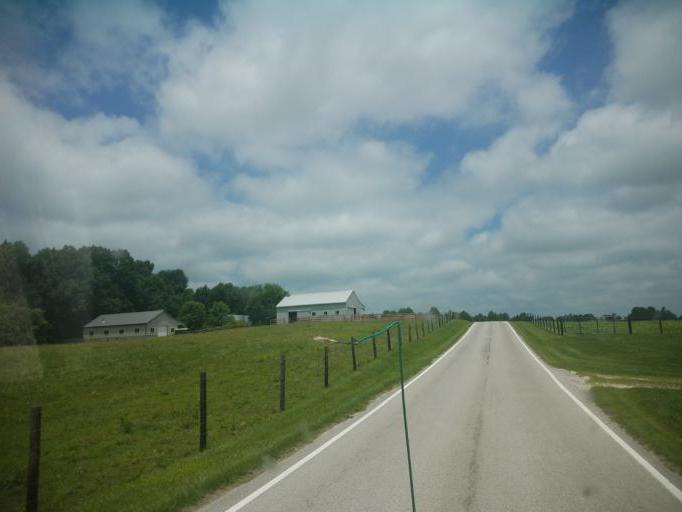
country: US
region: Kentucky
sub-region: Hart County
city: Munfordville
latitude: 37.3438
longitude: -86.0372
